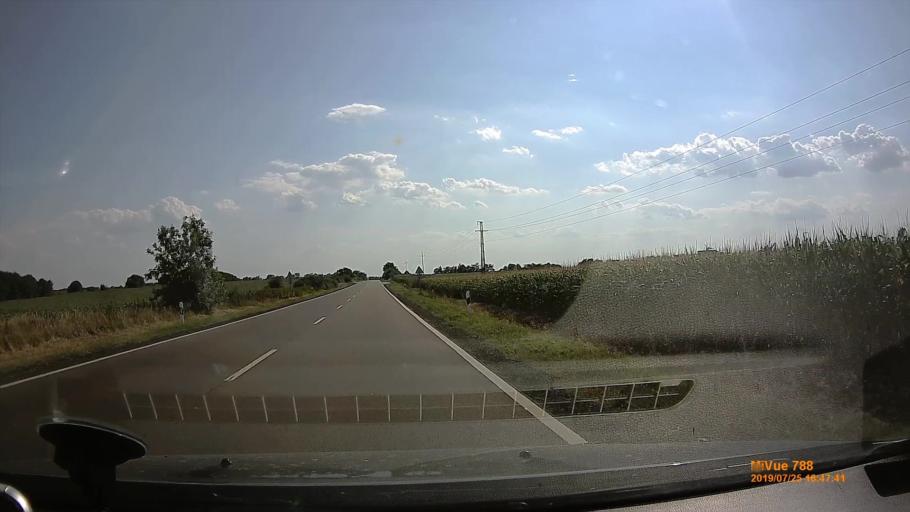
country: HU
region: Heves
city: Nagyrede
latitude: 47.7171
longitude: 19.8407
